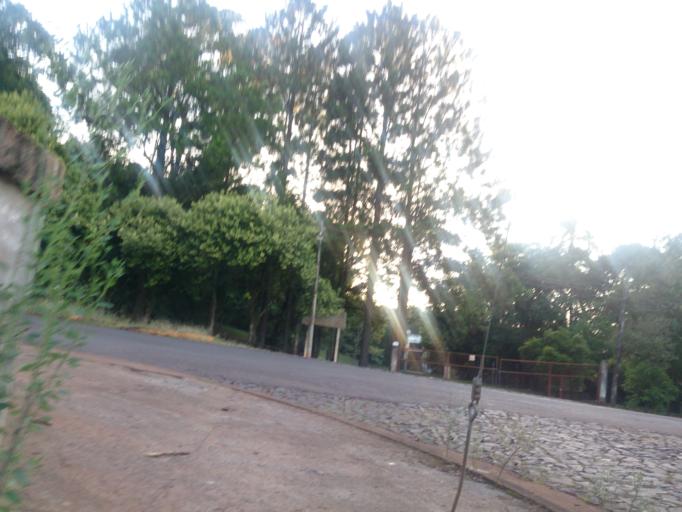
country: AR
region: Misiones
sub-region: Departamento de Obera
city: Obera
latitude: -27.4955
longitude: -55.1167
